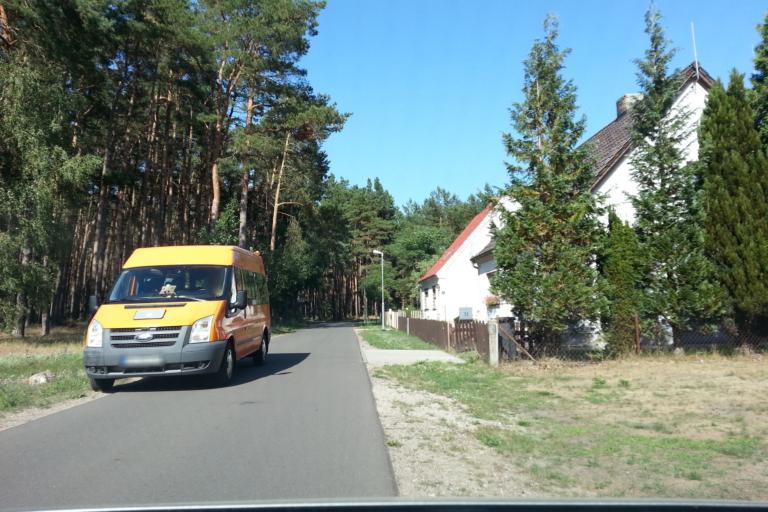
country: DE
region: Mecklenburg-Vorpommern
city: Eggesin
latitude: 53.6871
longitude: 14.0450
